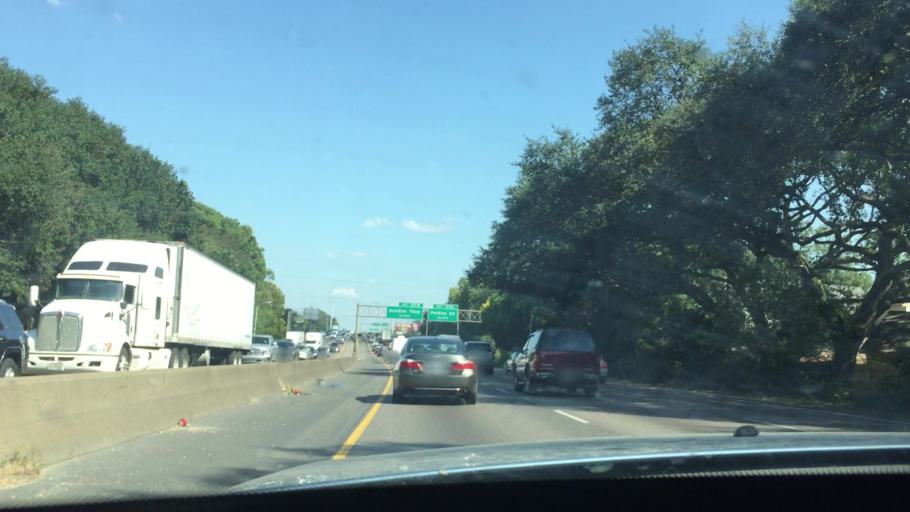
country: US
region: Louisiana
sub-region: East Baton Rouge Parish
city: Baton Rouge
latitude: 30.4255
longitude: -91.1635
